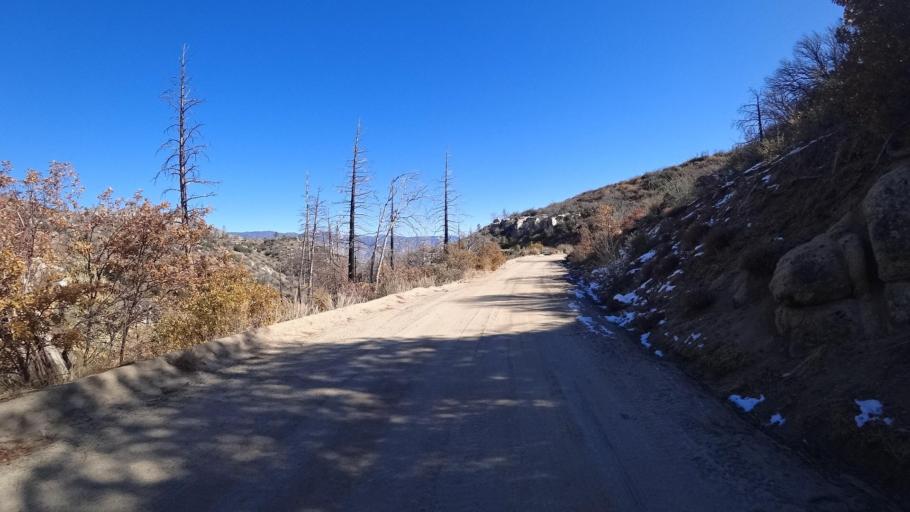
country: US
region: California
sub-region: Kern County
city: Alta Sierra
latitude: 35.7100
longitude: -118.5160
